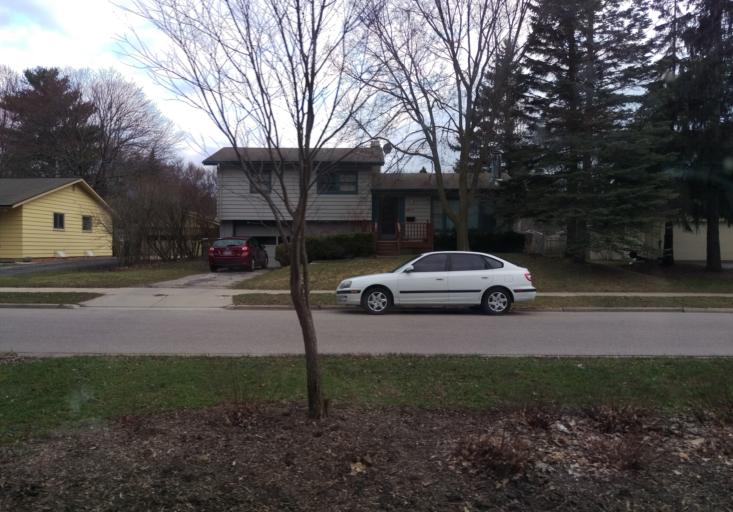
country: US
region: Wisconsin
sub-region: Dane County
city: Shorewood Hills
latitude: 43.0537
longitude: -89.4648
